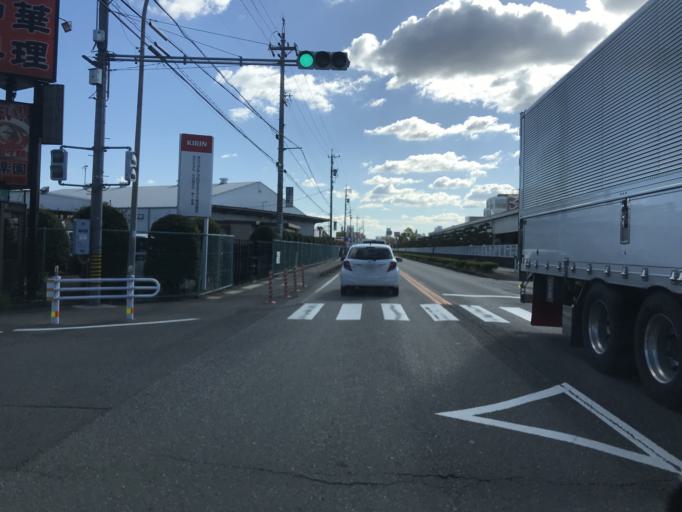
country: JP
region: Aichi
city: Nagoya-shi
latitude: 35.2122
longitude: 136.8511
